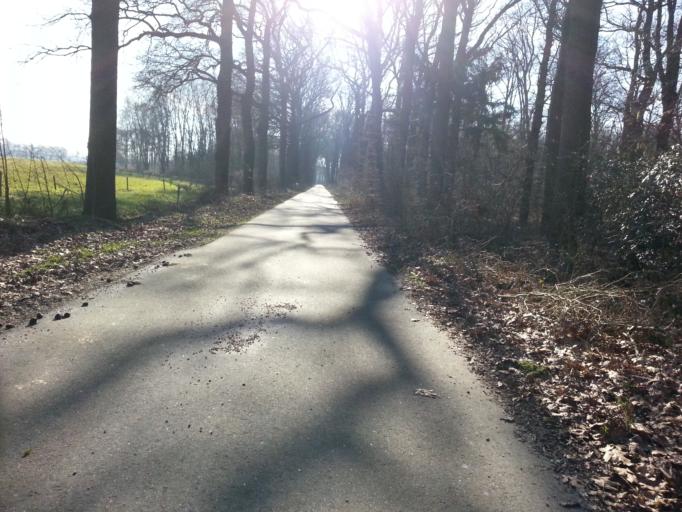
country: NL
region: Utrecht
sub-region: Gemeente Woudenberg
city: Woudenberg
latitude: 52.0656
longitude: 5.4393
